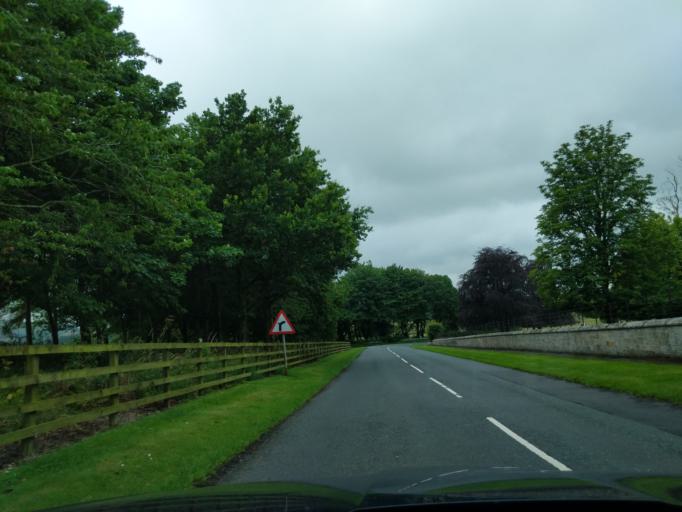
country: GB
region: England
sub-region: Northumberland
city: Ford
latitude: 55.6285
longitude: -2.0920
